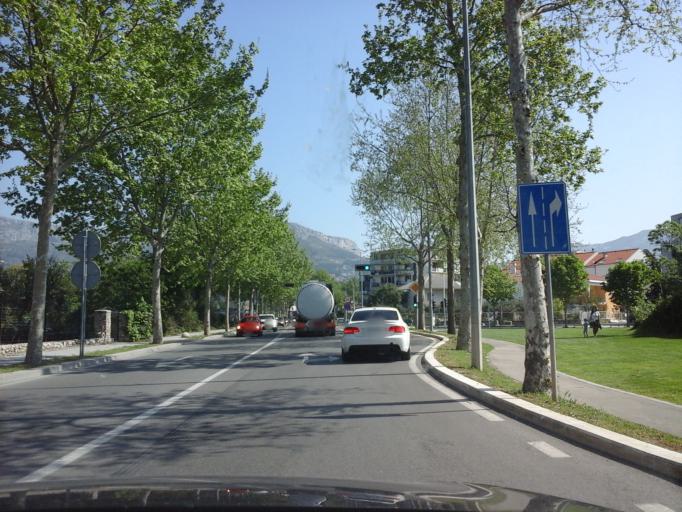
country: HR
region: Splitsko-Dalmatinska
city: Solin
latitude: 43.5384
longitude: 16.4889
